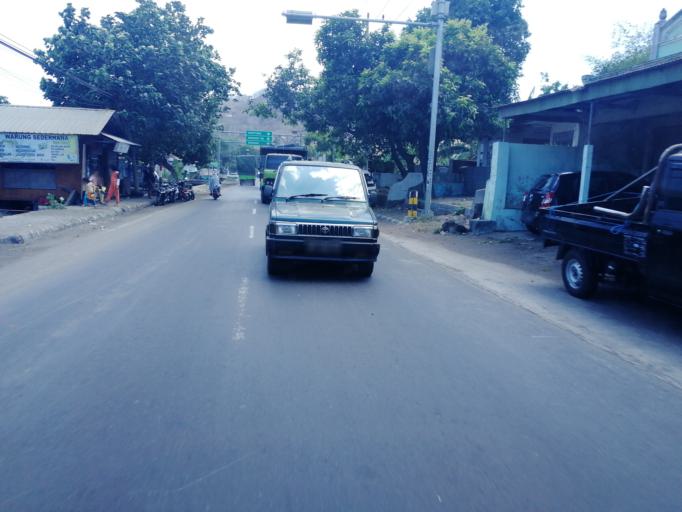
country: ID
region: West Nusa Tenggara
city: Jelateng Timur
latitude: -8.7258
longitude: 116.0755
